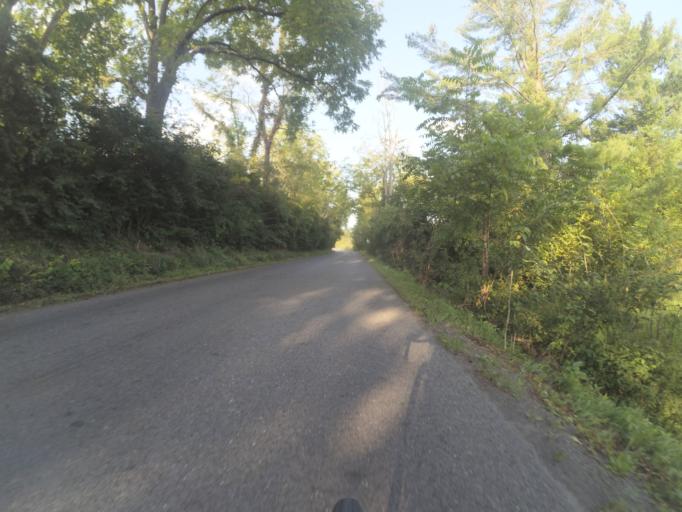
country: US
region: Pennsylvania
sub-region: Centre County
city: Centre Hall
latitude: 40.8145
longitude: -77.5988
